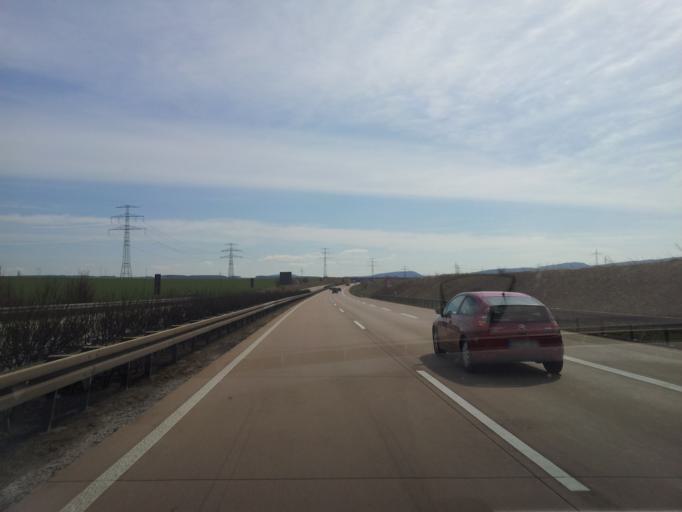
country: DE
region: Thuringia
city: Alkersleben
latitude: 50.8489
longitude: 11.0101
